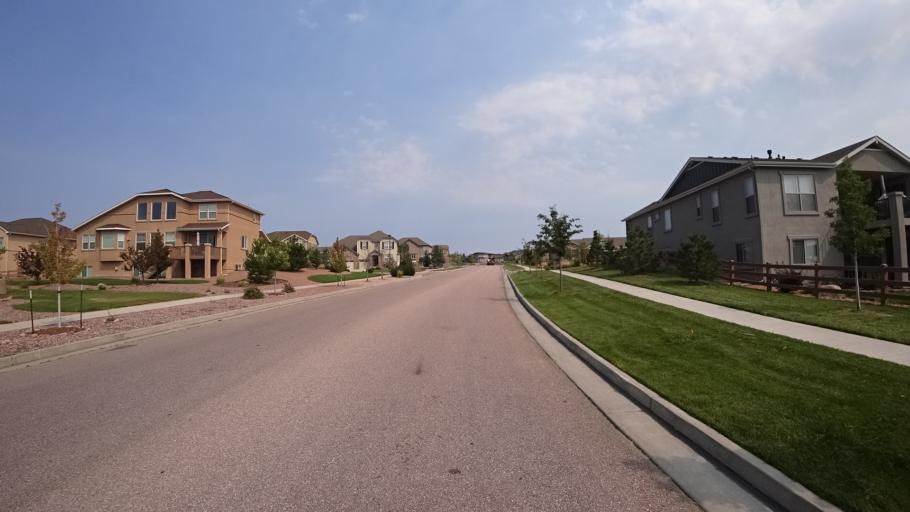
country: US
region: Colorado
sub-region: El Paso County
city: Black Forest
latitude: 38.9670
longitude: -104.7139
